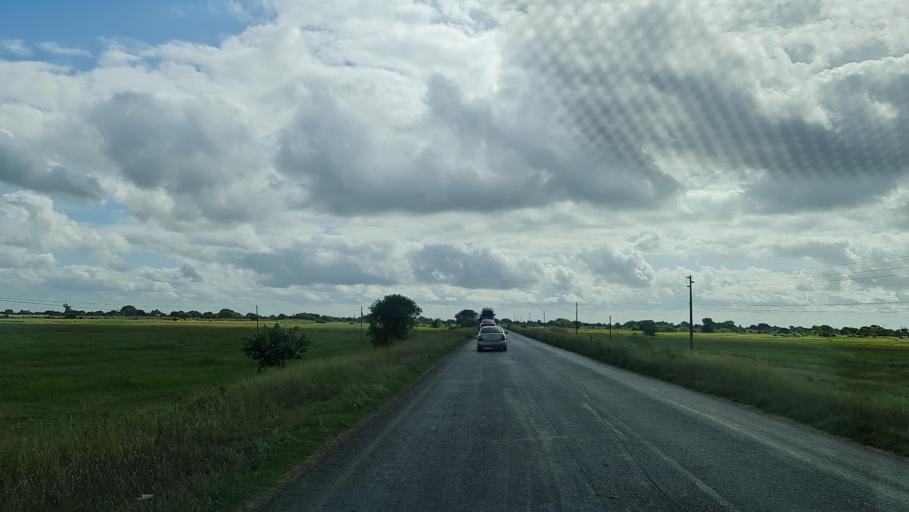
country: MZ
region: Gaza
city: Macia
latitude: -25.0941
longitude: 32.8342
